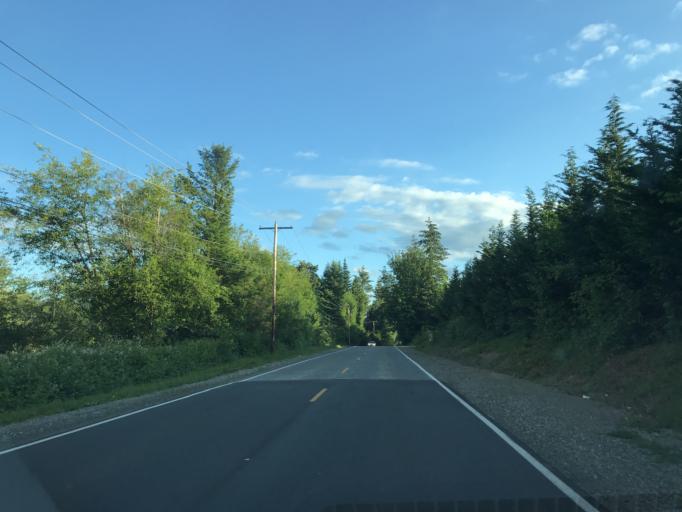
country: US
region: Washington
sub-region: King County
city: Black Diamond
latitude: 47.3148
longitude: -122.0097
